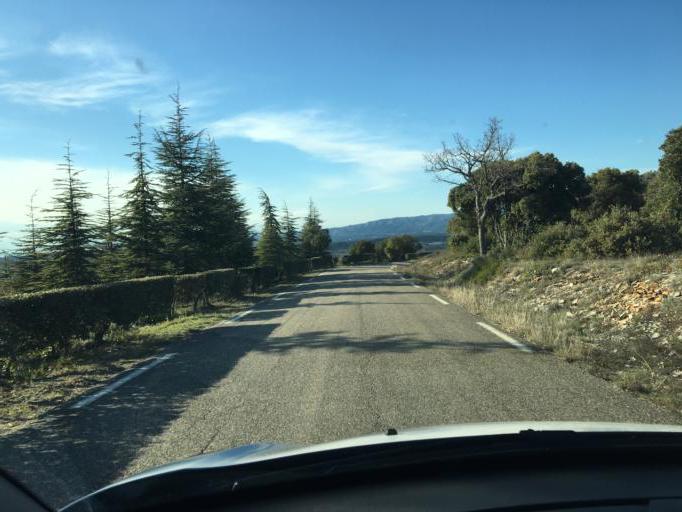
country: FR
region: Provence-Alpes-Cote d'Azur
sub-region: Departement du Vaucluse
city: Villes-sur-Auzon
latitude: 44.0426
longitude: 5.2463
